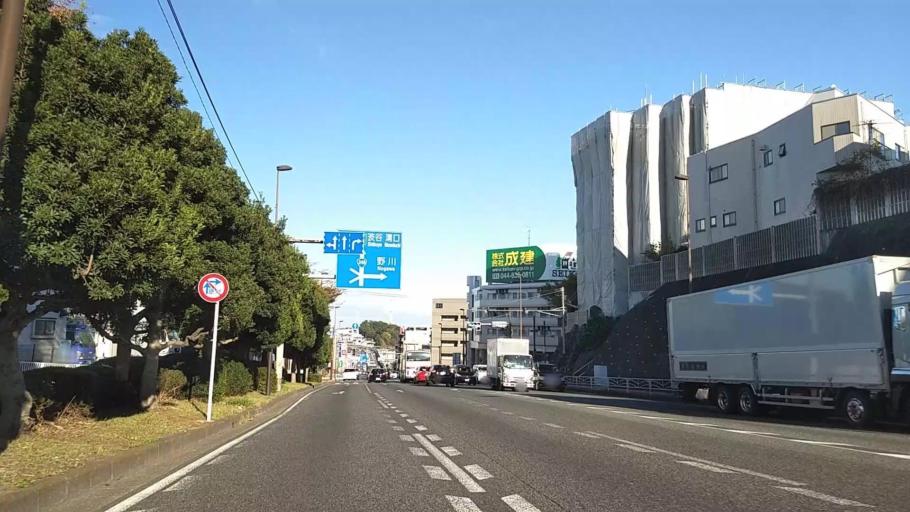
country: JP
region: Tokyo
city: Chofugaoka
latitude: 35.5795
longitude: 139.5908
